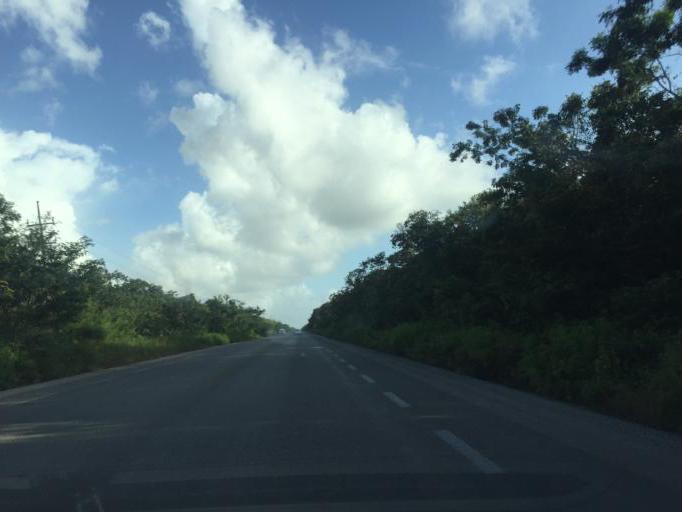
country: MX
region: Quintana Roo
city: Coba
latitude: 20.4762
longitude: -87.6914
